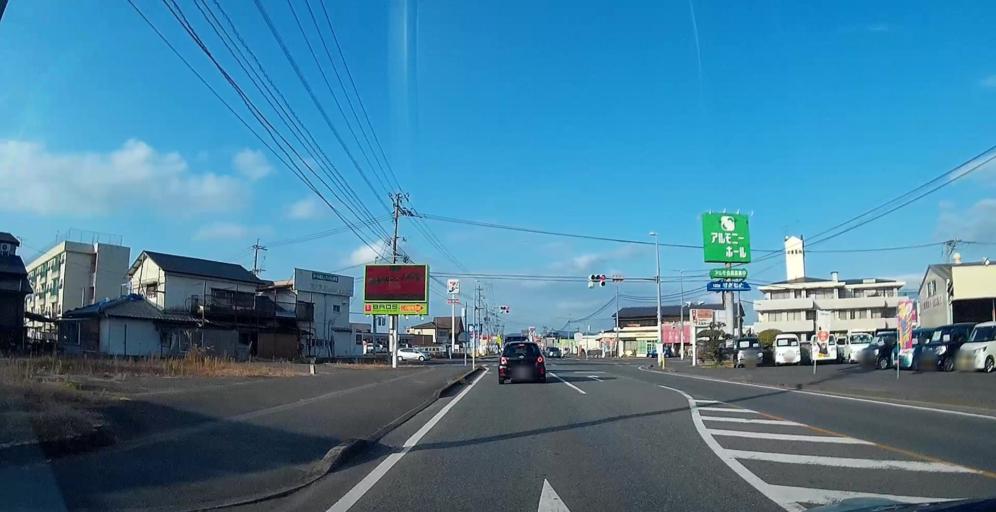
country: JP
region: Kumamoto
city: Matsubase
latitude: 32.5943
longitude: 130.7025
